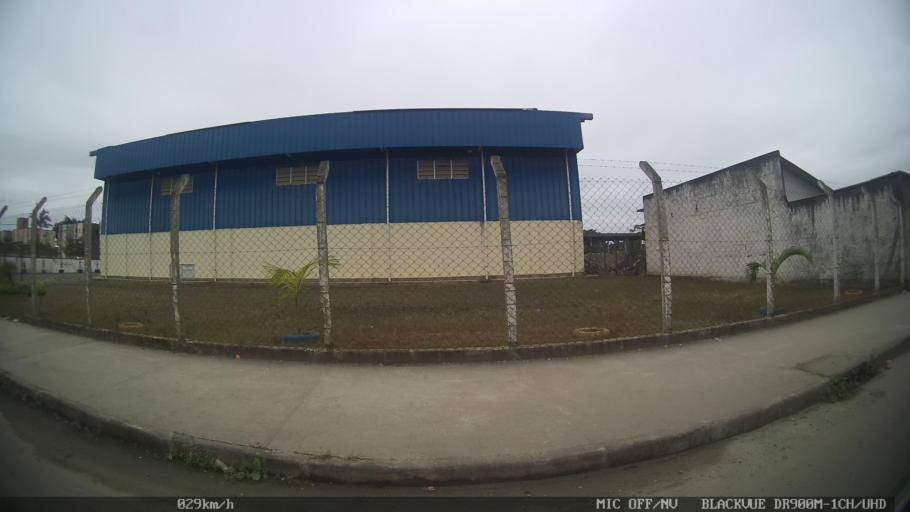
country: BR
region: Santa Catarina
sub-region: Joinville
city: Joinville
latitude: -26.2846
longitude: -48.9033
